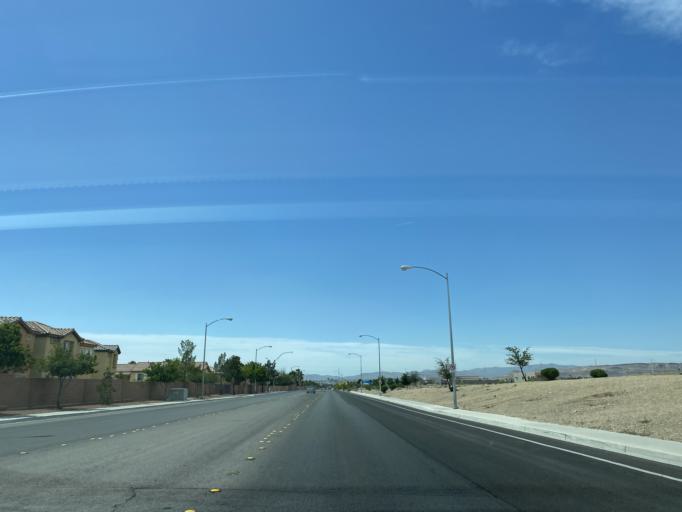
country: US
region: Nevada
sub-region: Clark County
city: Spring Valley
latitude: 36.1238
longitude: -115.2701
